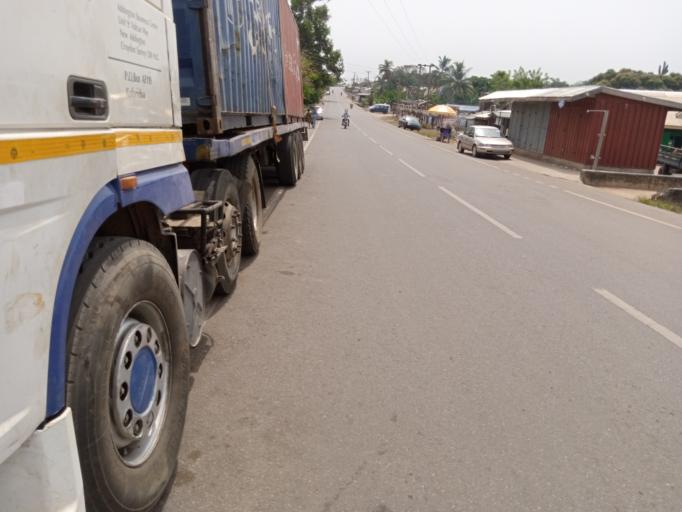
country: GH
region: Volta
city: Kpandu
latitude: 7.0075
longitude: 0.2957
